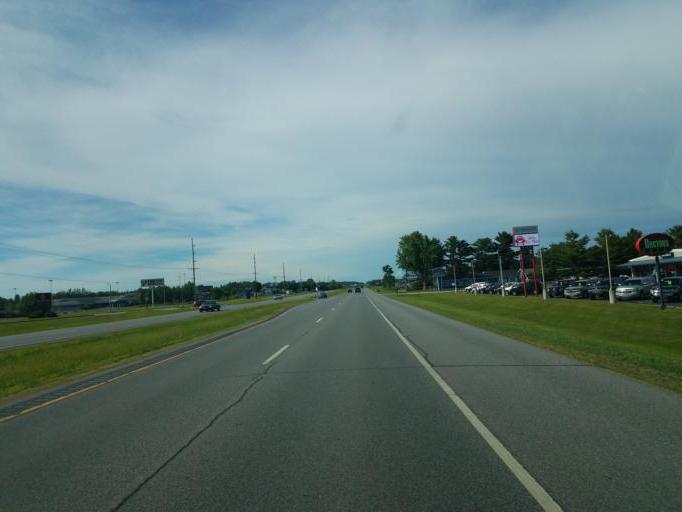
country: US
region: Wisconsin
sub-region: Monroe County
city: Tomah
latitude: 44.0049
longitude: -90.5048
